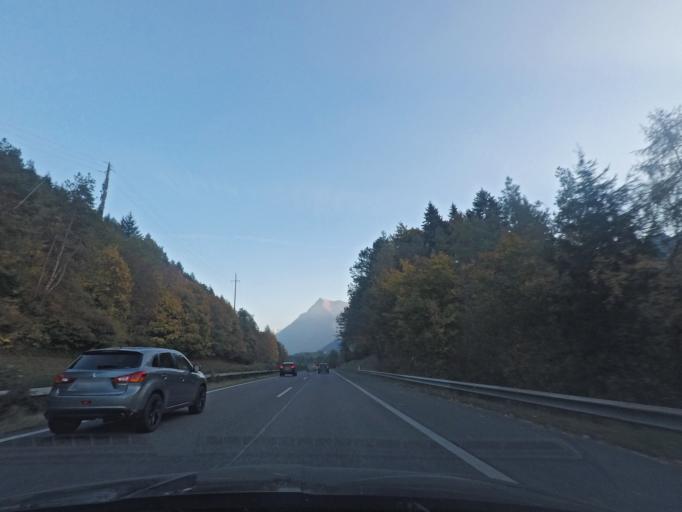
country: CH
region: Bern
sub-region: Thun District
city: Thun
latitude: 46.7235
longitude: 7.6077
